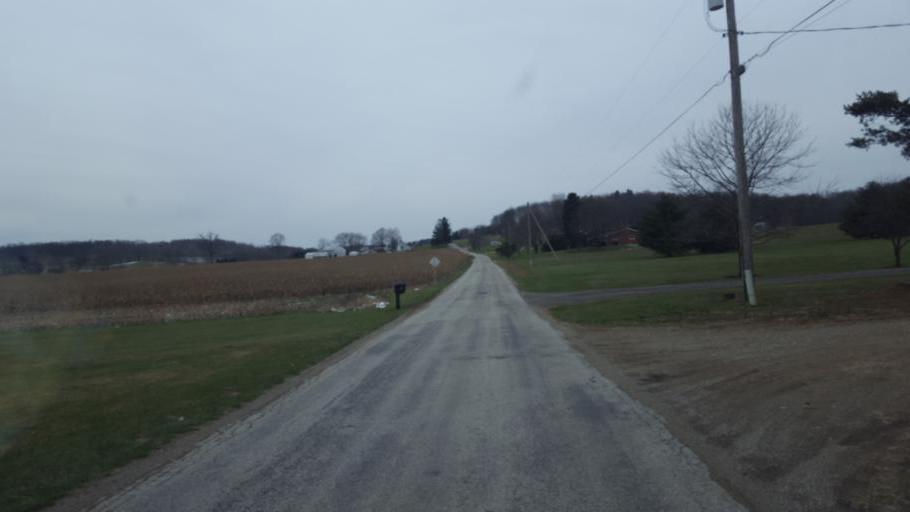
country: US
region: Ohio
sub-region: Sandusky County
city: Bellville
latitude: 40.5982
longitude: -82.5115
